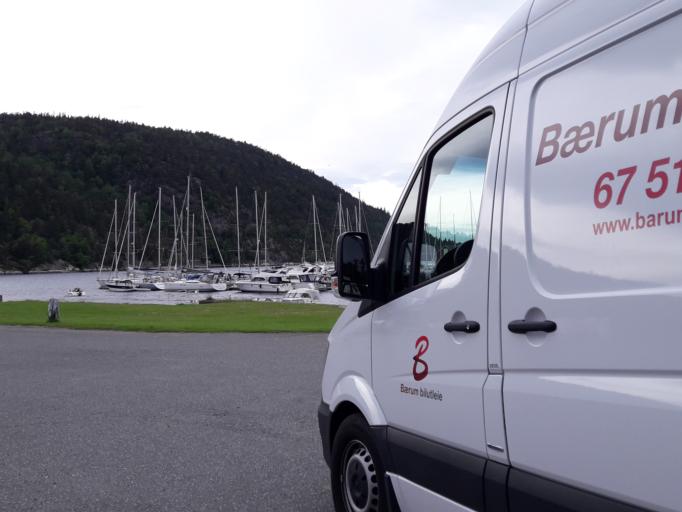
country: NO
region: Akershus
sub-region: Frogn
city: Drobak
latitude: 59.6763
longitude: 10.6060
